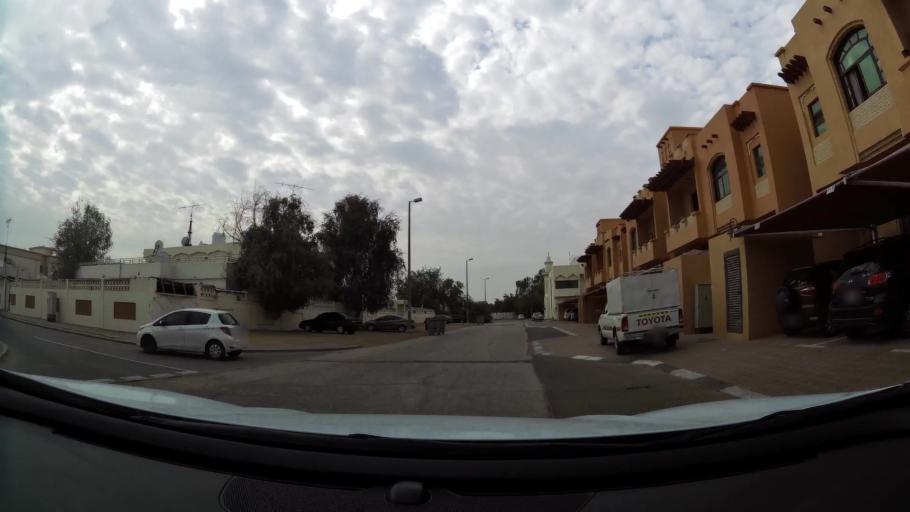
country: AE
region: Abu Dhabi
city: Al Ain
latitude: 24.2229
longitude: 55.7467
